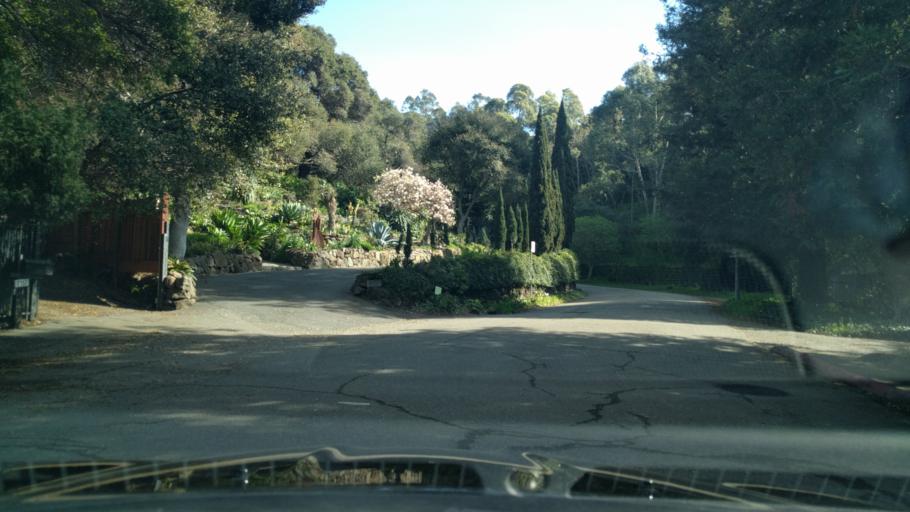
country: US
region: California
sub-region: Alameda County
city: Piedmont
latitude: 37.8506
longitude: -122.2369
